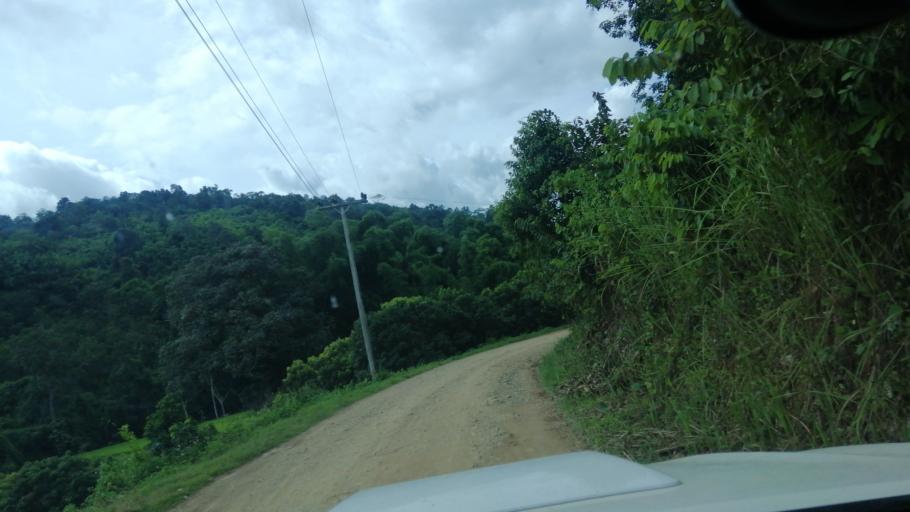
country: TH
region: Phayao
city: Phu Sang
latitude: 19.6001
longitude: 100.5338
